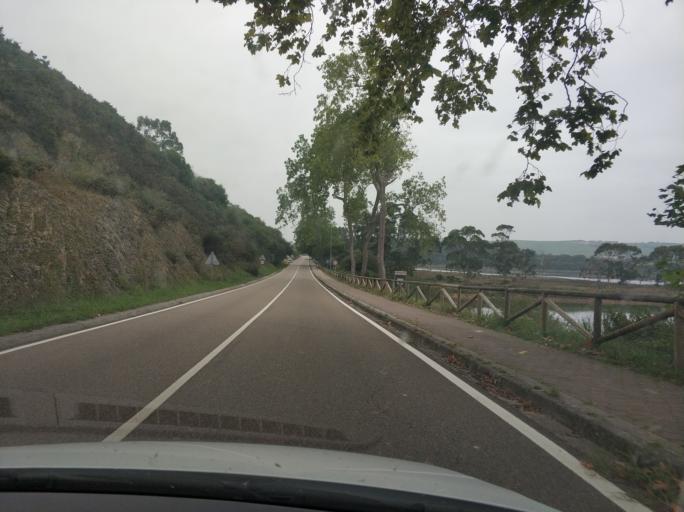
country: ES
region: Cantabria
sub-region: Provincia de Cantabria
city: Comillas
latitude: 43.3847
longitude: -4.3222
